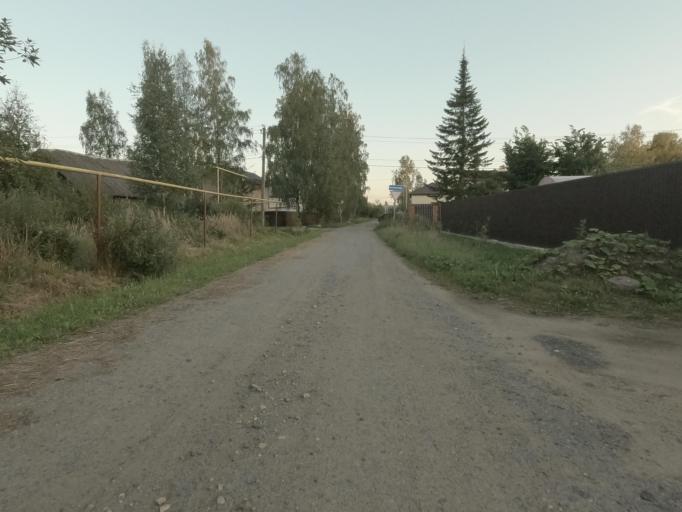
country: RU
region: Leningrad
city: Mga
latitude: 59.7599
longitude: 31.0495
